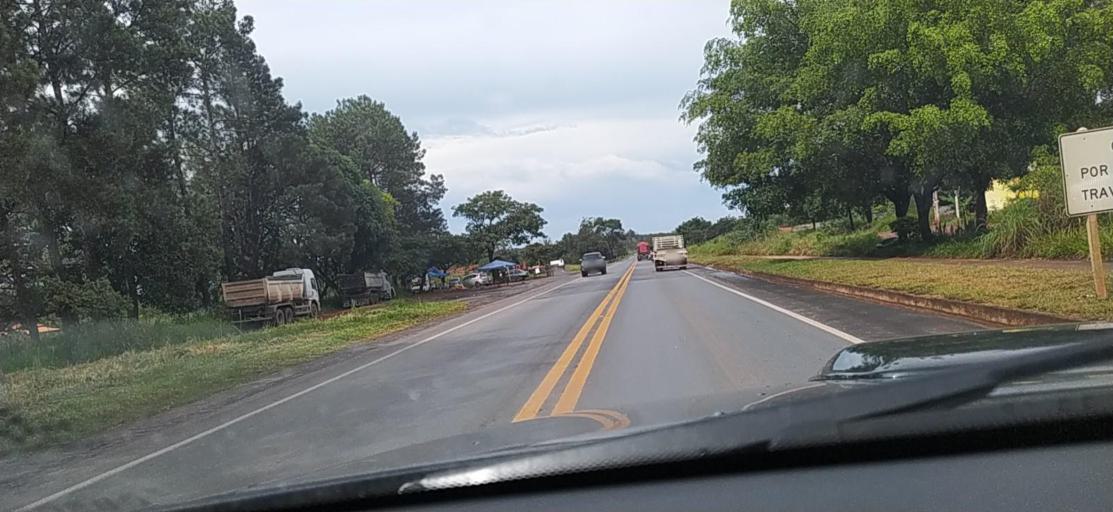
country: BR
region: Minas Gerais
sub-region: Montes Claros
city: Montes Claros
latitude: -16.8772
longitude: -43.8610
